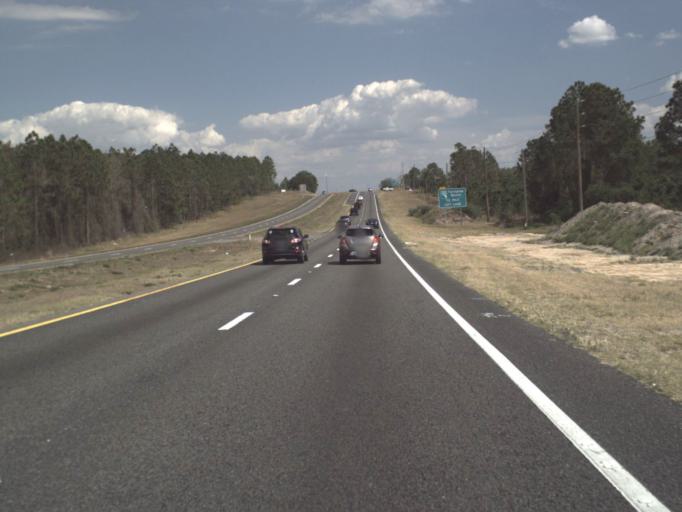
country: US
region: Florida
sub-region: Lake County
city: Howie In The Hills
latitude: 28.6450
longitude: -81.8189
